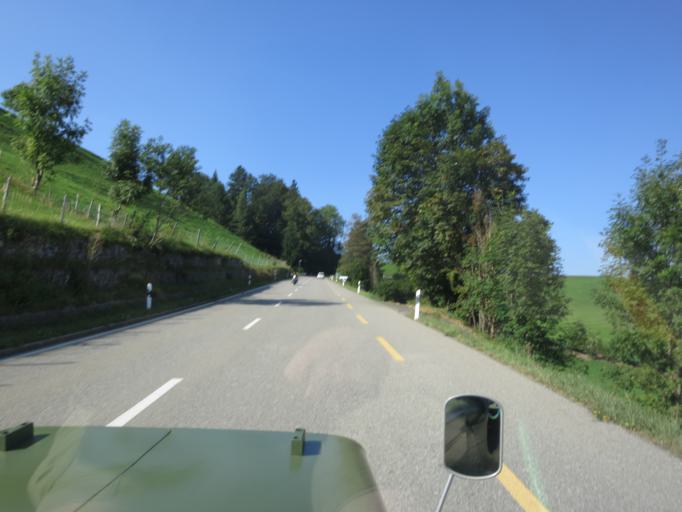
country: CH
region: Zurich
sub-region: Bezirk Hinwil
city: Wald
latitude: 47.3042
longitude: 8.9136
